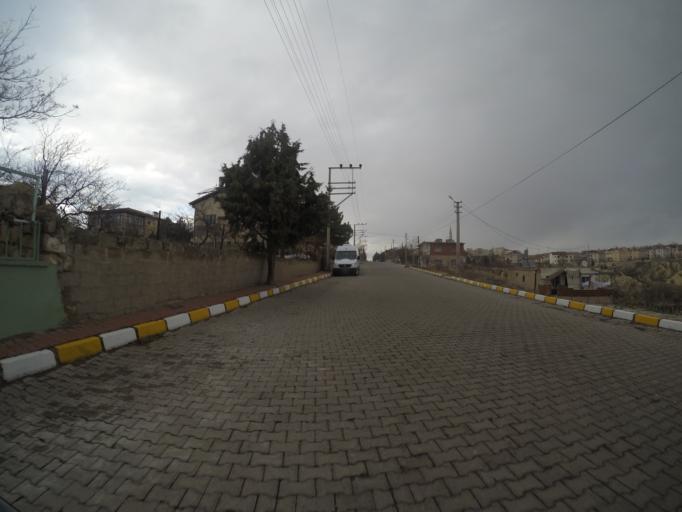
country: TR
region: Nevsehir
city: Goereme
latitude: 38.6276
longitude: 34.8596
